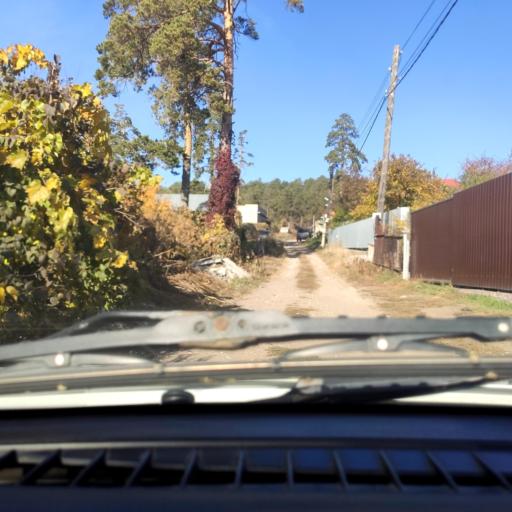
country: RU
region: Samara
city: Zhigulevsk
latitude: 53.4692
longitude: 49.5877
